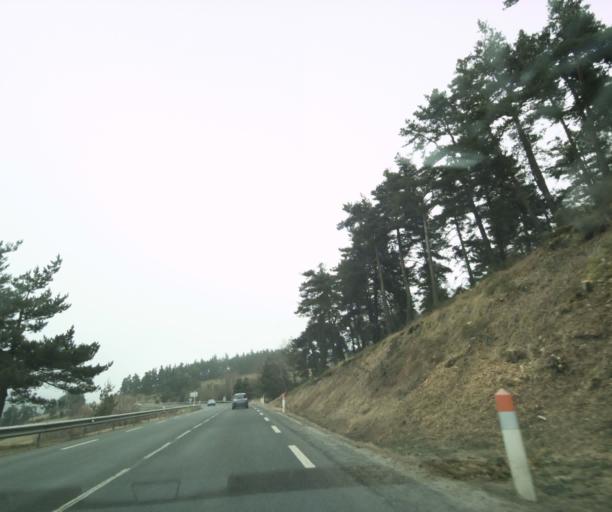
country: FR
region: Languedoc-Roussillon
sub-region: Departement de la Lozere
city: Langogne
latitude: 44.6704
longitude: 3.7638
